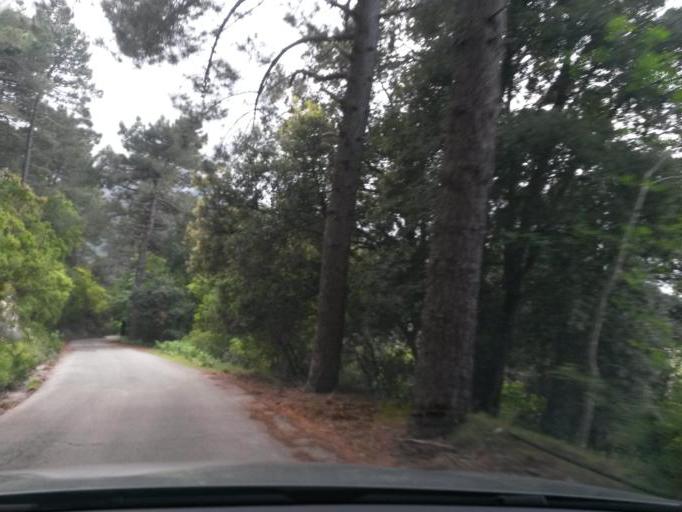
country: IT
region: Tuscany
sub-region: Provincia di Livorno
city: Marciana Marina
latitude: 42.7805
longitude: 10.1900
